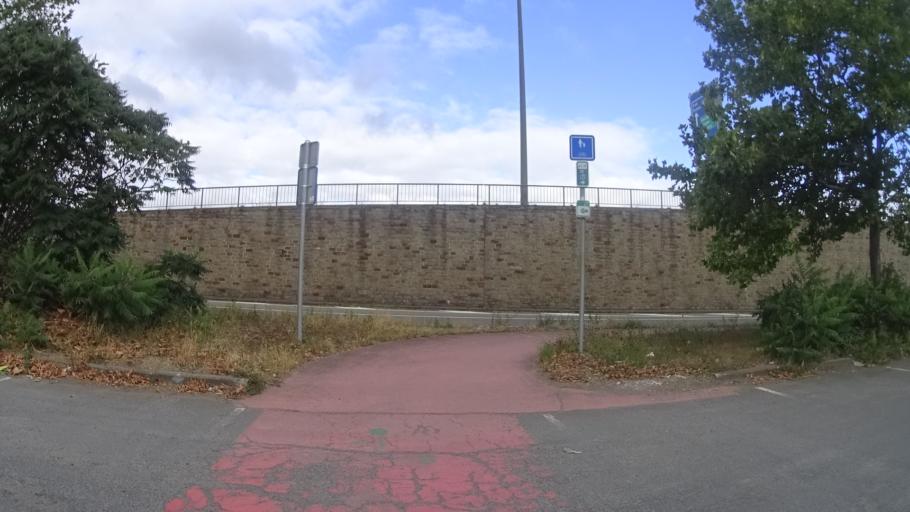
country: BE
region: Wallonia
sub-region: Province de Liege
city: Herstal
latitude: 50.6792
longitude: 5.6427
